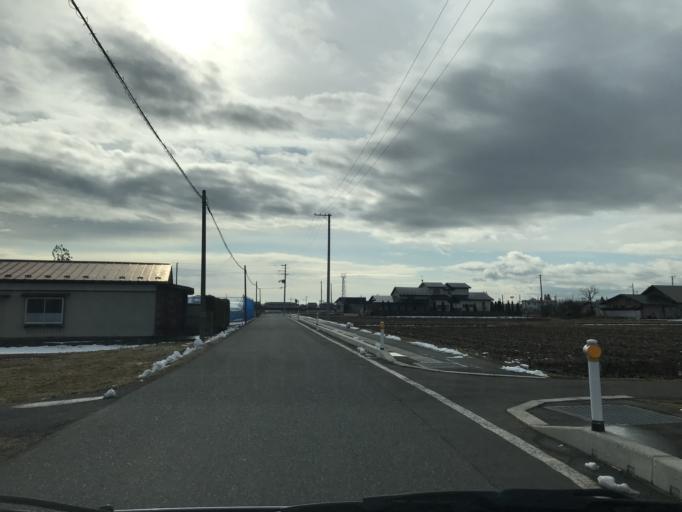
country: JP
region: Iwate
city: Mizusawa
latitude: 39.1778
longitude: 141.1332
